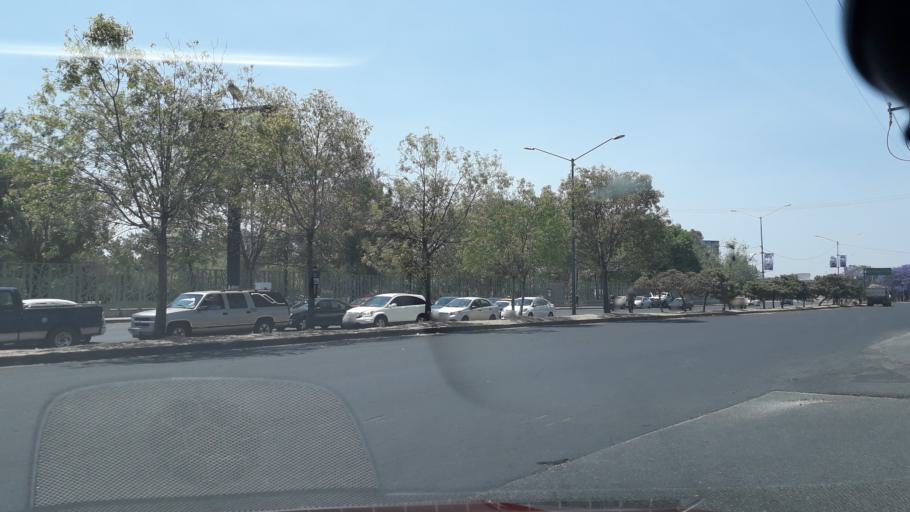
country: MX
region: Puebla
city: Puebla
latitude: 19.0251
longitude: -98.1910
